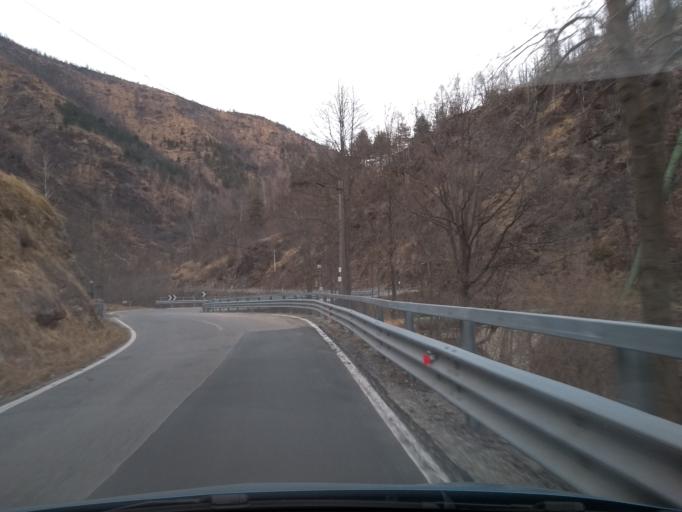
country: IT
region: Piedmont
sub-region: Provincia di Torino
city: La Villa
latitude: 45.2438
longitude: 7.4339
